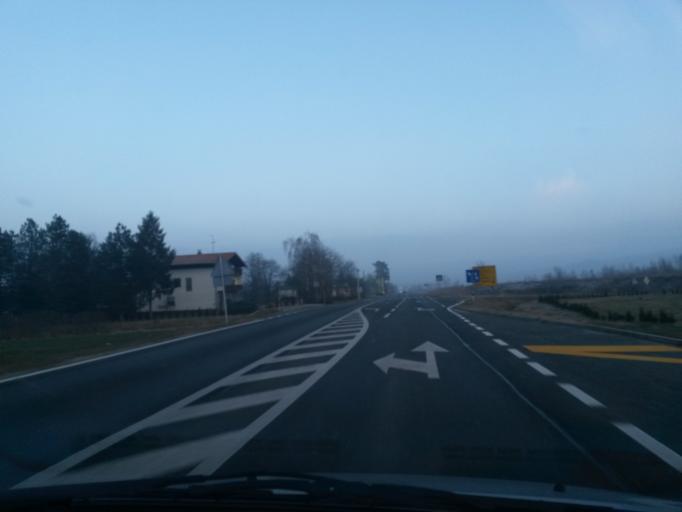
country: HR
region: Koprivnicko-Krizevacka
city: Reka
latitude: 46.1996
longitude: 16.7161
